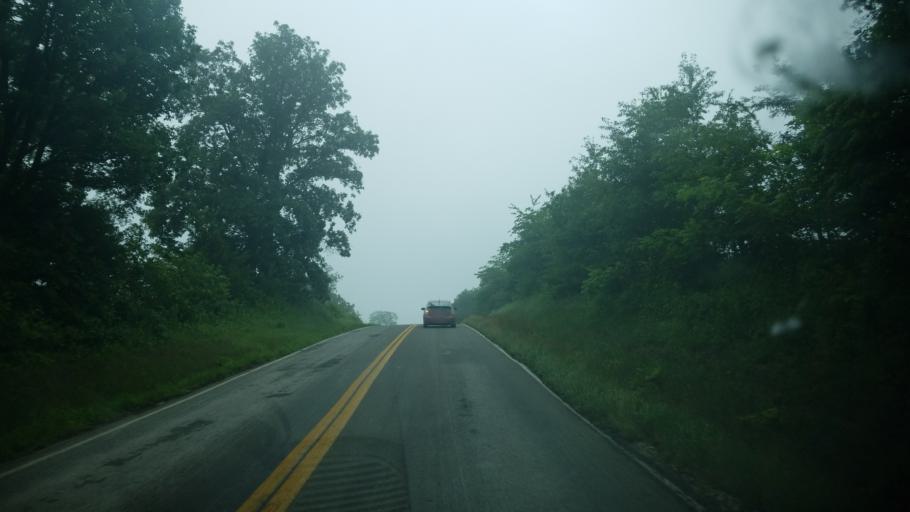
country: US
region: Missouri
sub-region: Audrain County
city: Vandalia
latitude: 39.3111
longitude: -91.3450
